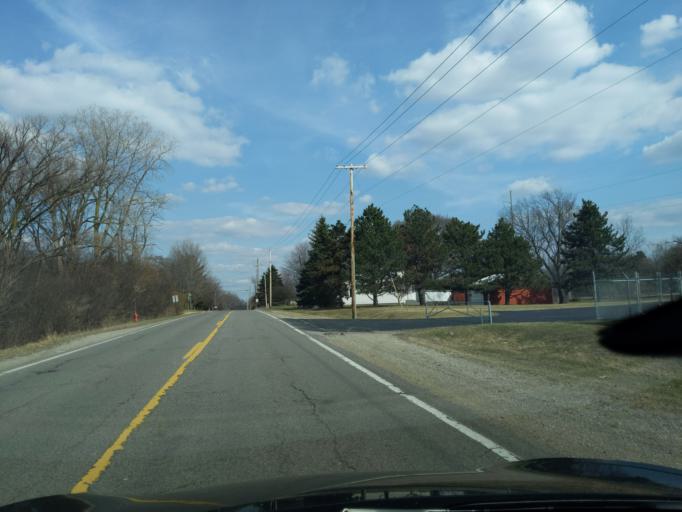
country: US
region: Michigan
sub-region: Jackson County
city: Jackson
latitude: 42.2736
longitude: -84.4219
